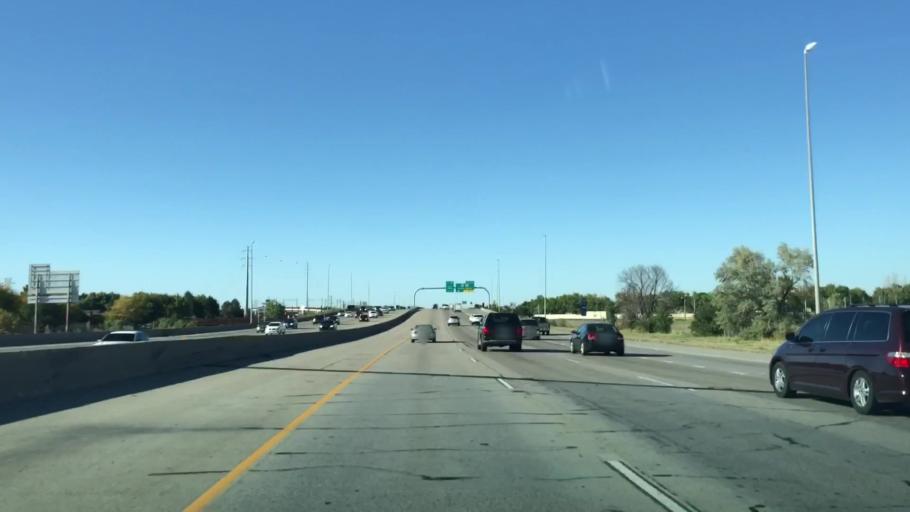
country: US
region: Colorado
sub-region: Adams County
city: Aurora
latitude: 39.7332
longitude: -104.8253
